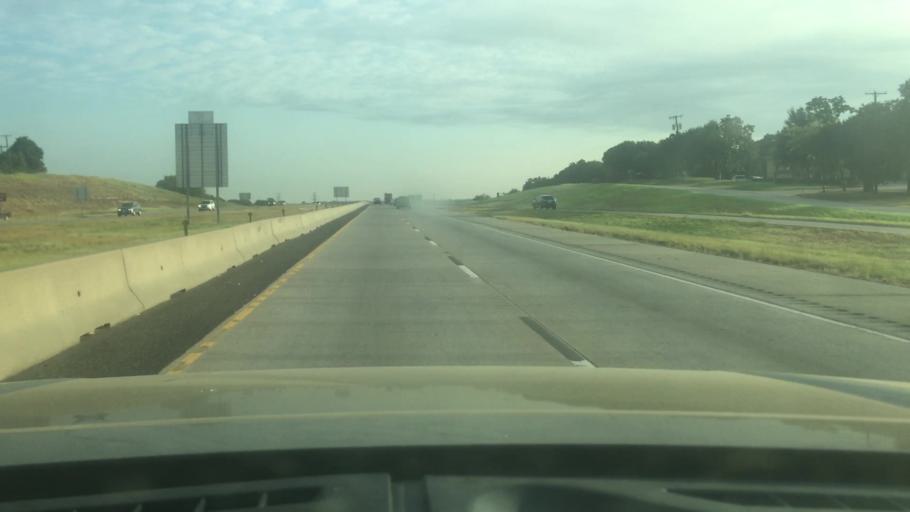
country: US
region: Texas
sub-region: Tarrant County
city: Euless
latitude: 32.8543
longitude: -97.1089
